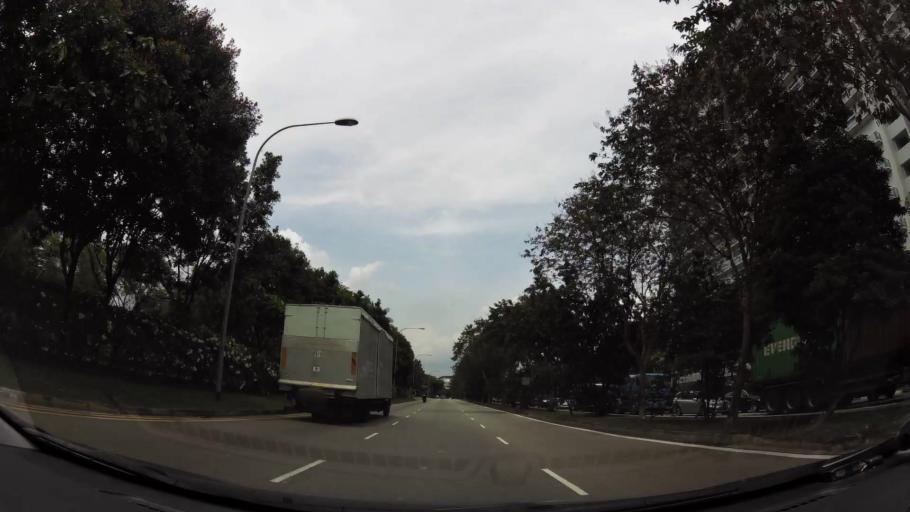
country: SG
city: Singapore
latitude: 1.3160
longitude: 103.6959
